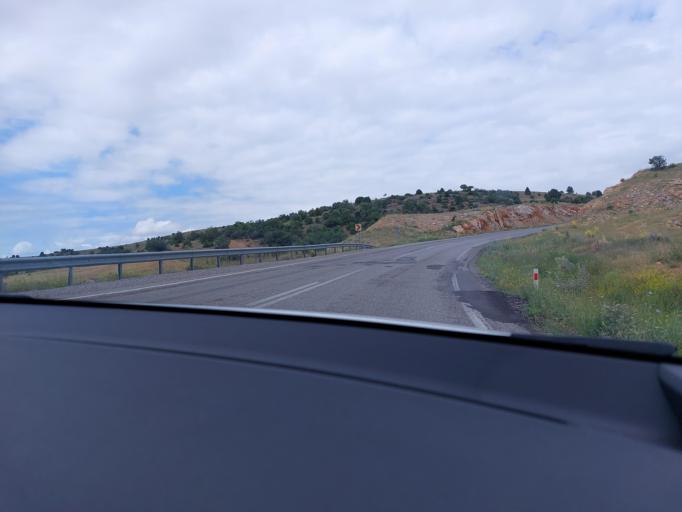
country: TR
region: Konya
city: Doganbey
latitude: 37.8937
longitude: 31.8005
